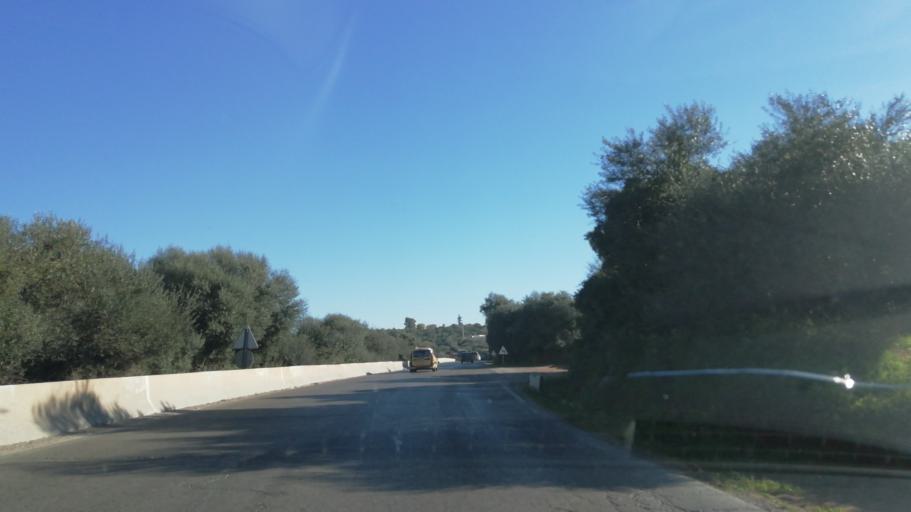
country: DZ
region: Relizane
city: Smala
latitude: 35.7018
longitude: 0.7716
